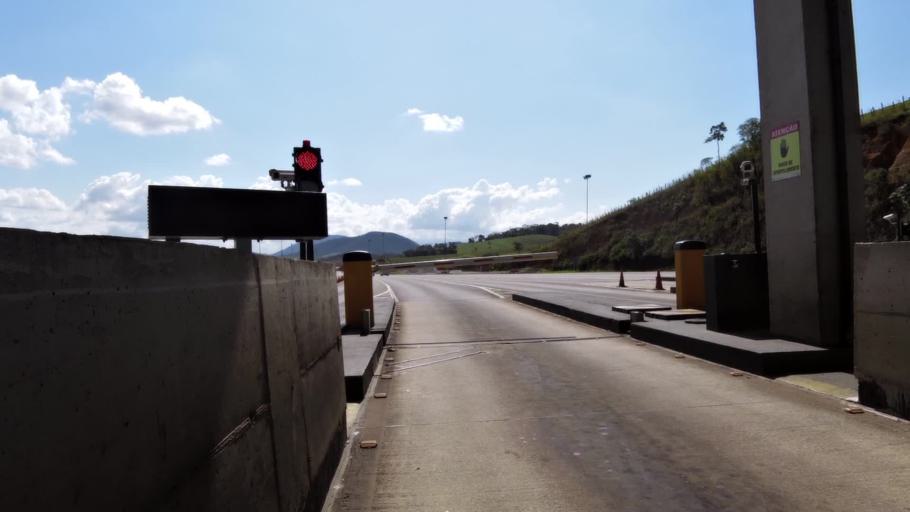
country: BR
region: Rio de Janeiro
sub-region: Macae
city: Macae
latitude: -22.0493
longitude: -41.6847
